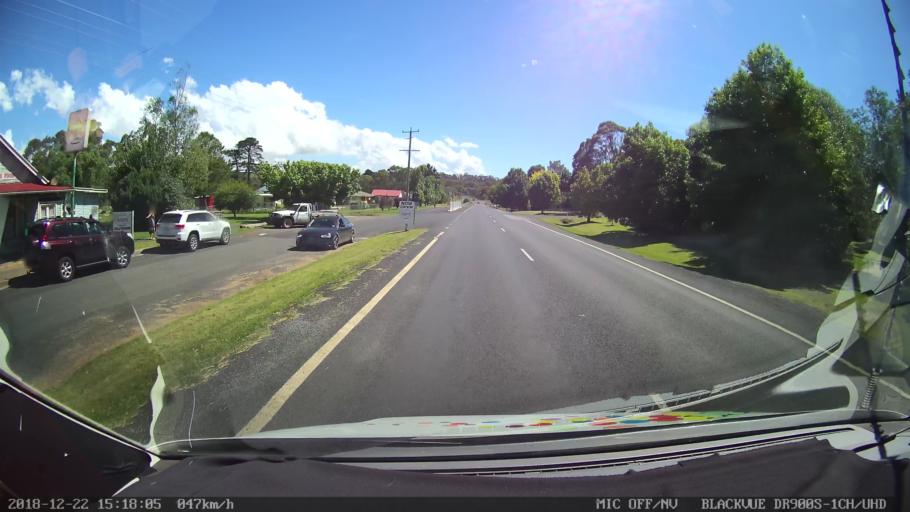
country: AU
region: New South Wales
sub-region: Bellingen
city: Dorrigo
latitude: -30.4017
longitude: 152.3498
